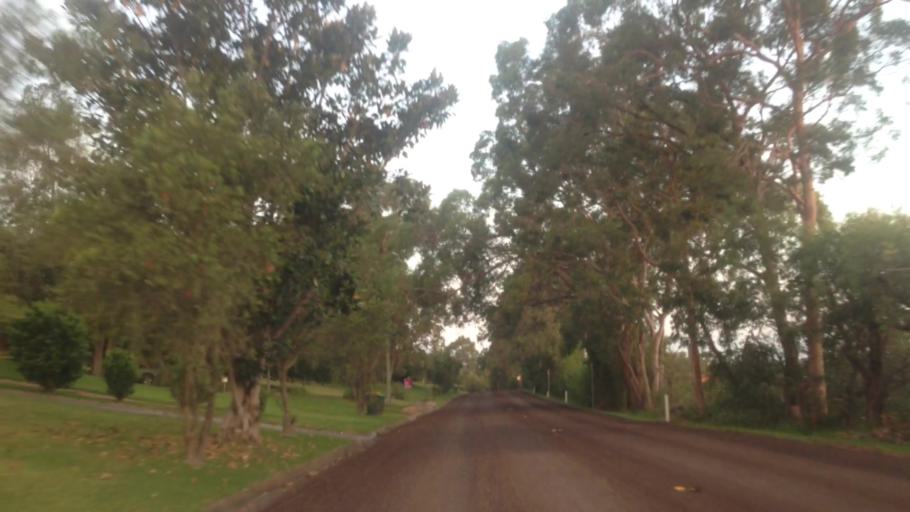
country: AU
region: New South Wales
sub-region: Lake Macquarie Shire
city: Dora Creek
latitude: -33.0780
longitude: 151.4905
